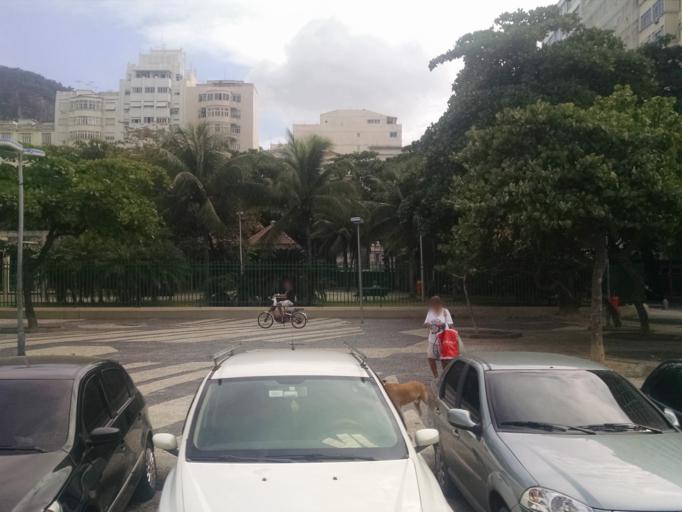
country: BR
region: Rio de Janeiro
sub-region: Rio De Janeiro
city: Rio de Janeiro
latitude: -22.9651
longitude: -43.1744
